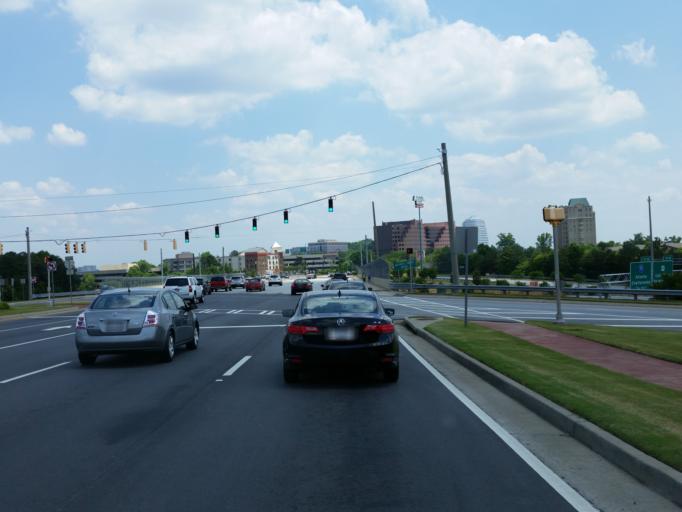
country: US
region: Georgia
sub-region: Cobb County
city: Vinings
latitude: 33.8632
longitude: -84.4811
